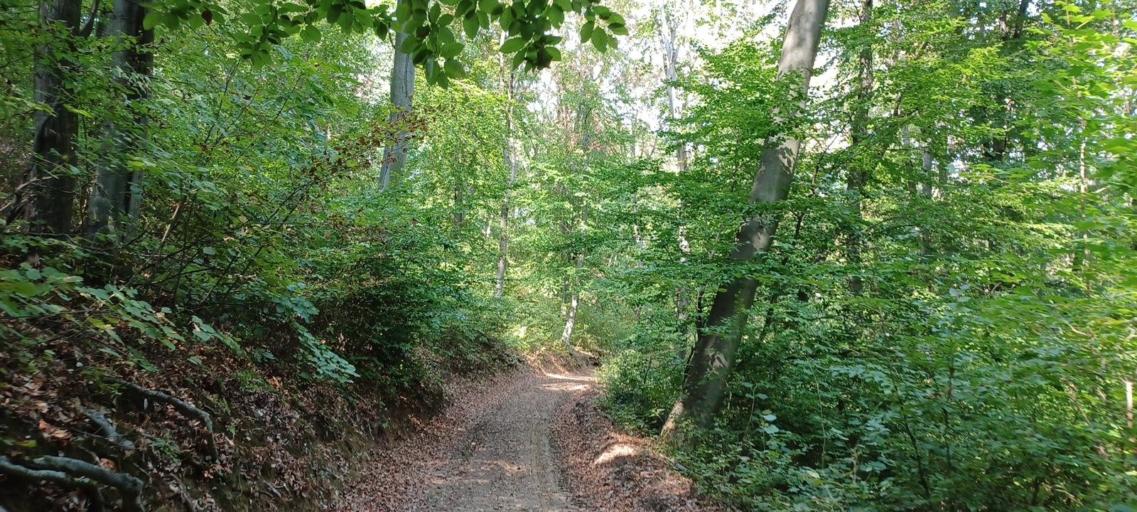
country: HU
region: Tolna
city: Szentgalpuszta
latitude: 46.3251
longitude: 18.6247
